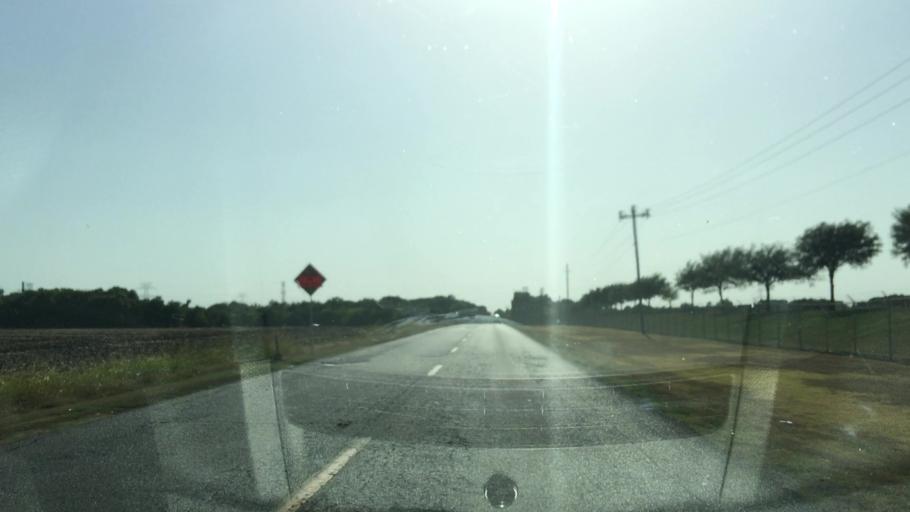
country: US
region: Texas
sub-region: Dallas County
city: Lancaster
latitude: 32.5611
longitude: -96.7714
